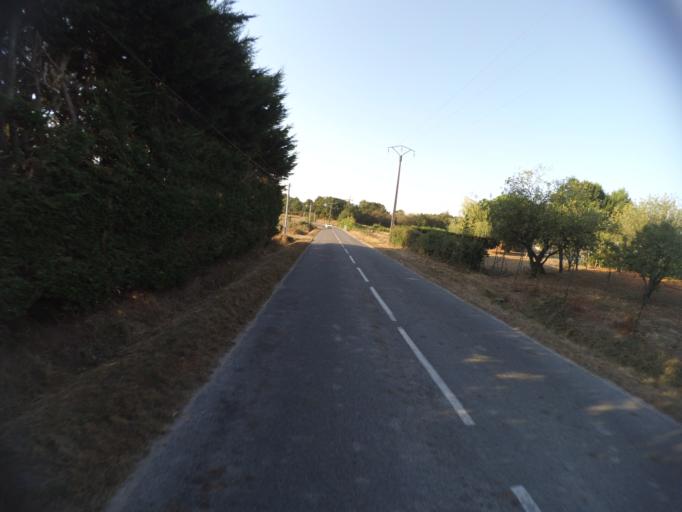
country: FR
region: Pays de la Loire
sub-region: Departement de la Loire-Atlantique
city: Aigrefeuille-sur-Maine
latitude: 47.0571
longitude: -1.4129
